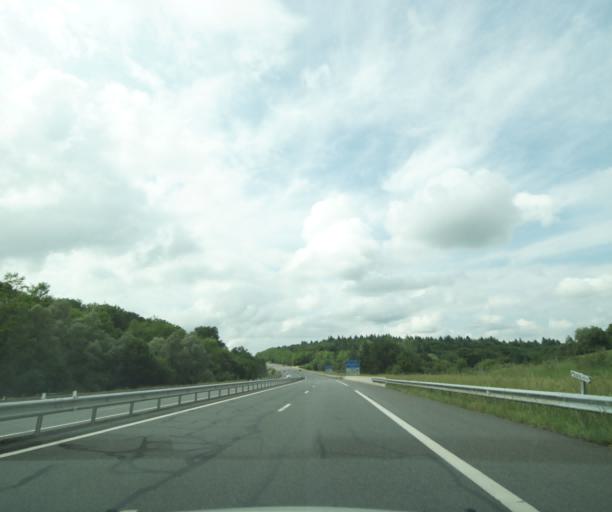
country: FR
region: Centre
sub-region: Departement du Cher
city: Orval
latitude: 46.7424
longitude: 2.4269
